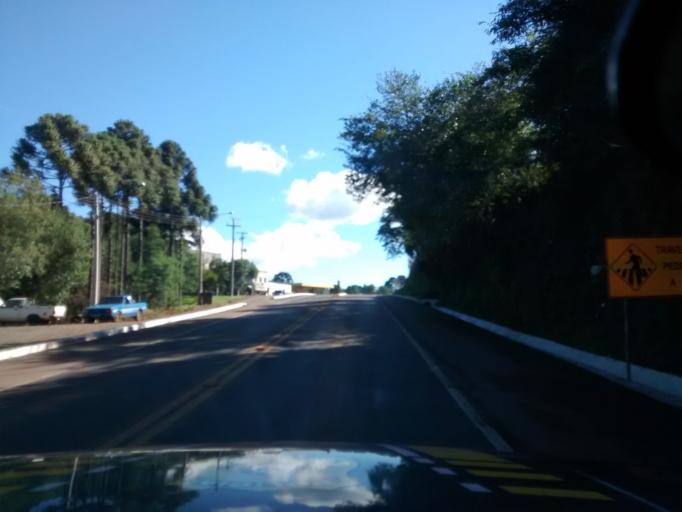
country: BR
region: Rio Grande do Sul
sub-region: Vacaria
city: Vacaria
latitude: -28.3253
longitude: -51.1857
